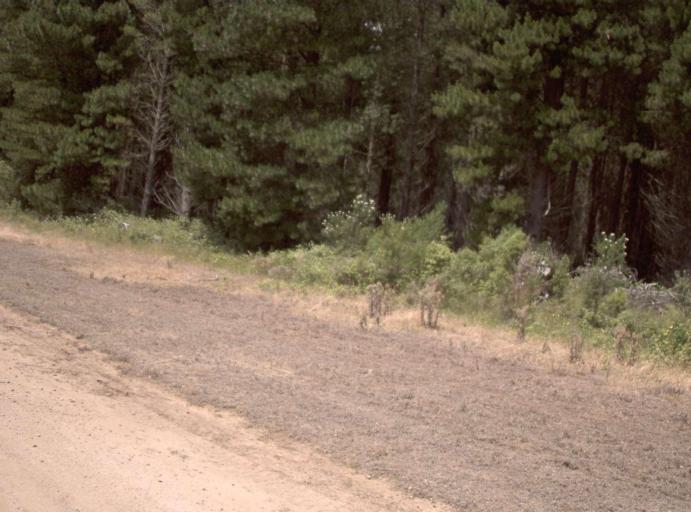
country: AU
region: Victoria
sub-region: Latrobe
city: Traralgon
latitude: -38.3976
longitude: 146.6569
